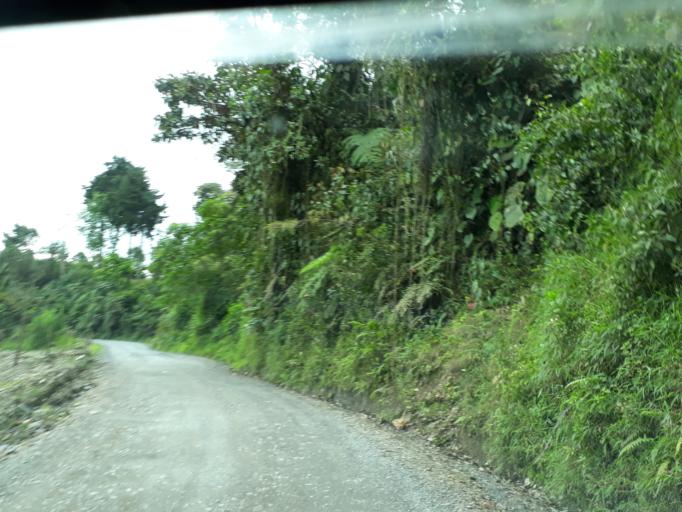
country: CO
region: Cundinamarca
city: Pacho
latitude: 5.2589
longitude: -74.1809
